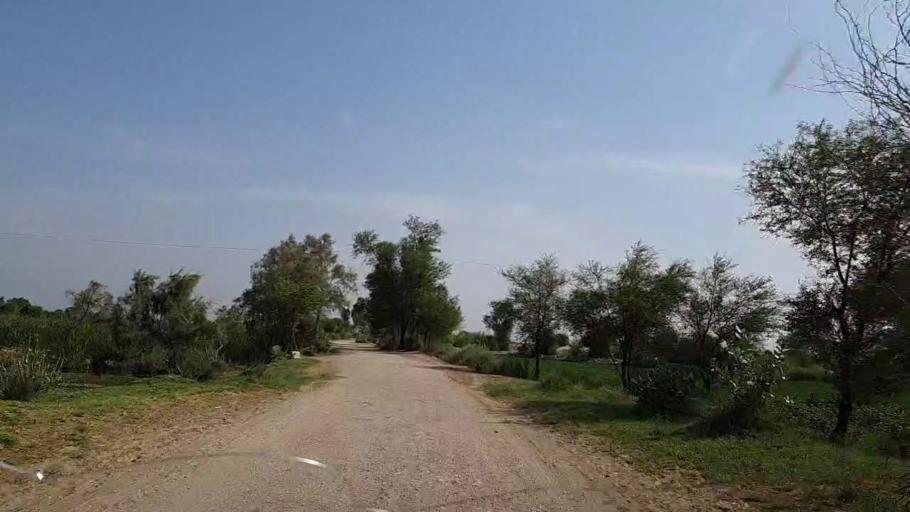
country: PK
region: Sindh
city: Khanpur
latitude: 27.7273
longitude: 69.3597
